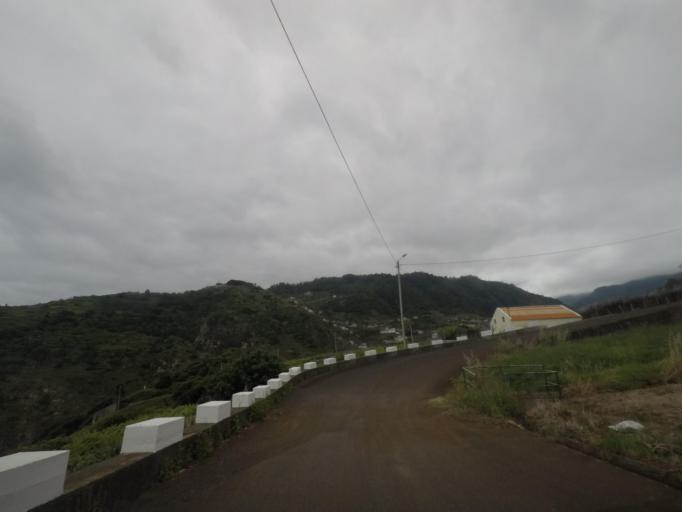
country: PT
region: Madeira
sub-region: Porto Moniz
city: Porto Moniz
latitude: 32.8555
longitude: -17.1588
